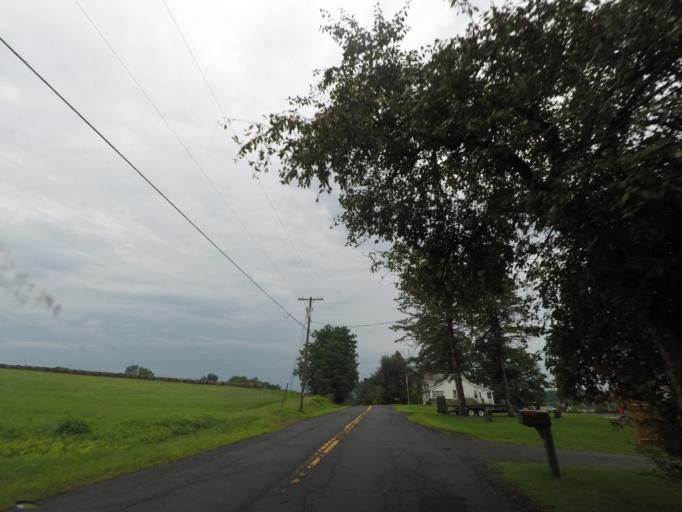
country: US
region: New York
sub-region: Rensselaer County
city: Poestenkill
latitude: 42.8044
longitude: -73.5675
